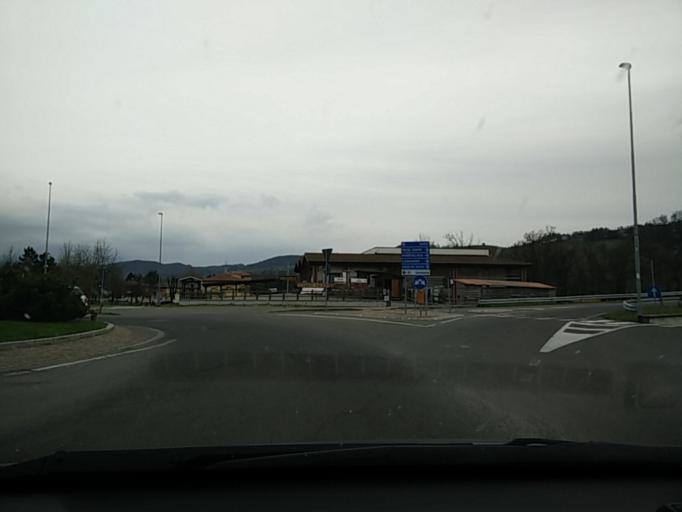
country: IT
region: Lombardy
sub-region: Provincia di Pavia
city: Godiasco
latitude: 44.8997
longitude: 9.0531
